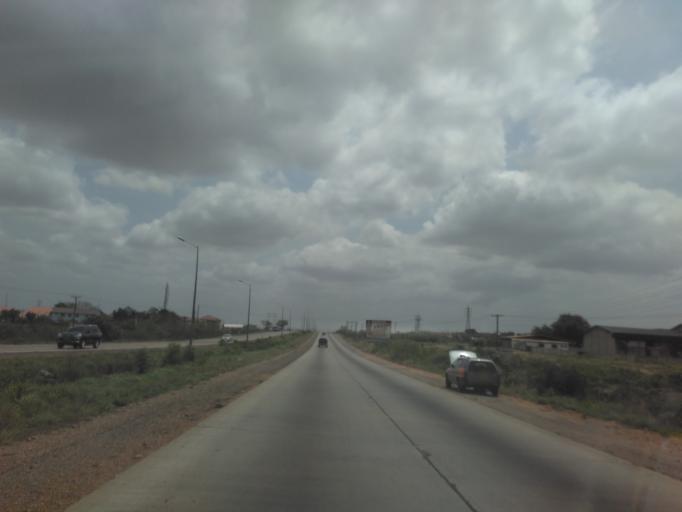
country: GH
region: Greater Accra
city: Nungua
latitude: 5.6516
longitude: -0.1017
